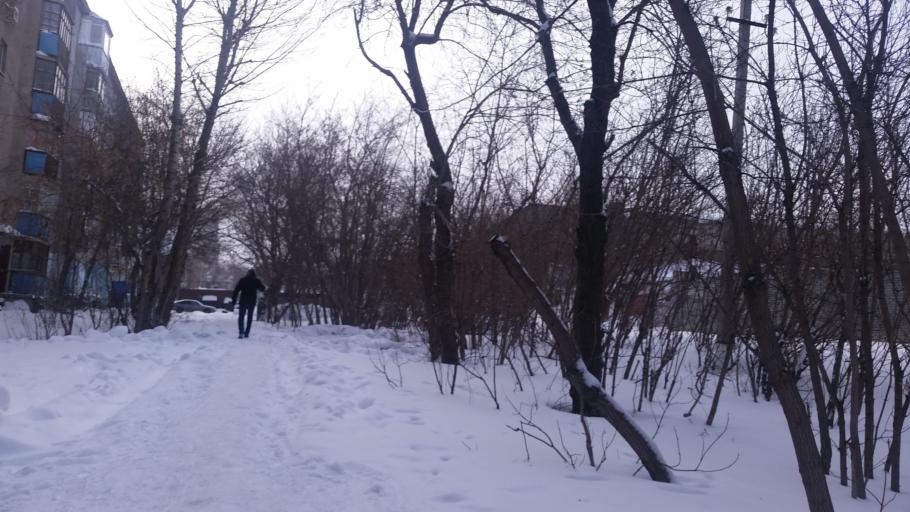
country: KZ
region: Astana Qalasy
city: Astana
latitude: 51.1681
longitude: 71.4613
